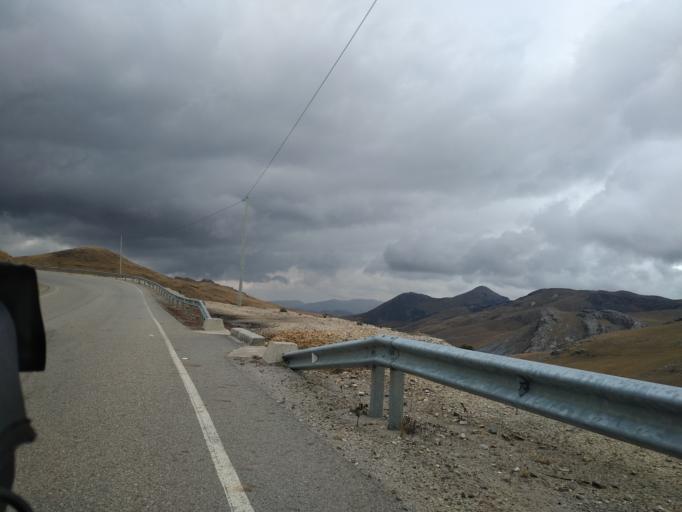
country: PE
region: La Libertad
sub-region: Provincia de Santiago de Chuco
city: Quiruvilca
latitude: -7.9886
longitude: -78.2810
